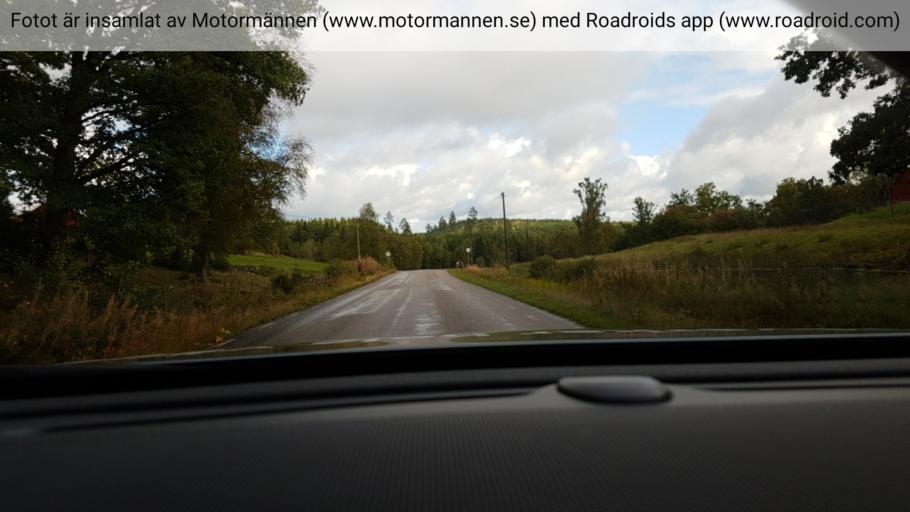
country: SE
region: Vaestra Goetaland
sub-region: Marks Kommun
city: Fritsla
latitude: 57.4195
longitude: 12.9268
